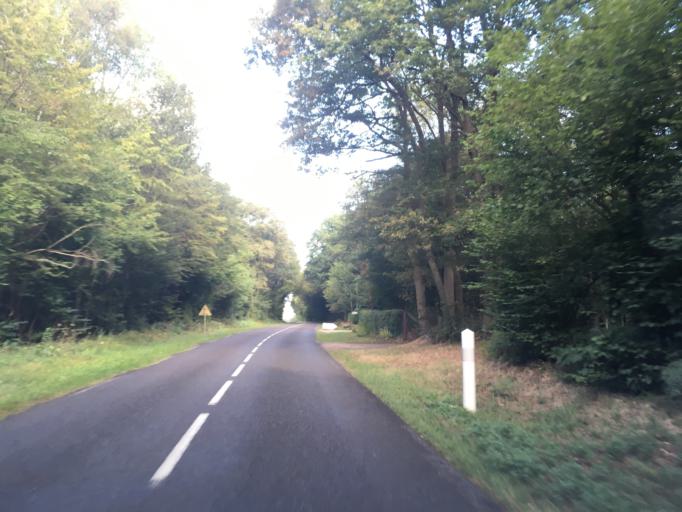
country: FR
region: Haute-Normandie
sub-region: Departement de l'Eure
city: Courcelles-sur-Seine
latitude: 49.1805
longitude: 1.3876
